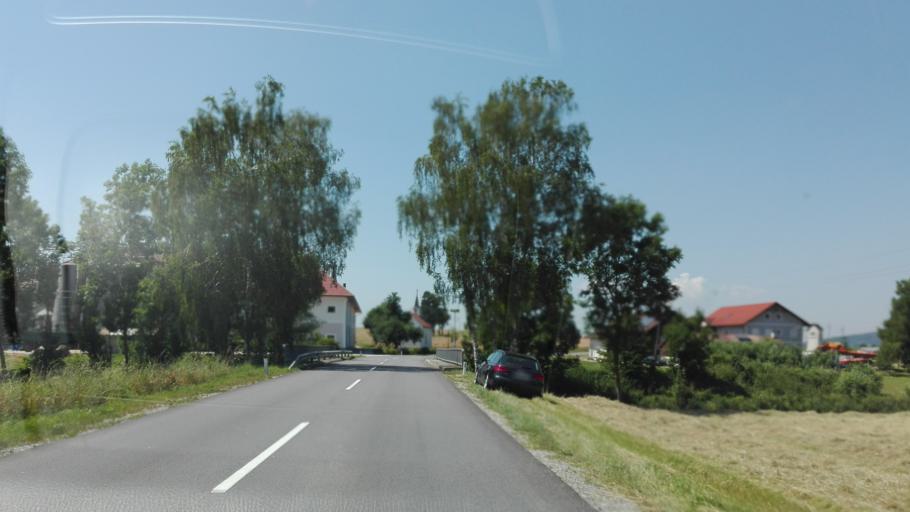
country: AT
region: Upper Austria
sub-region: Politischer Bezirk Grieskirchen
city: Grieskirchen
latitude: 48.3462
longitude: 13.8695
